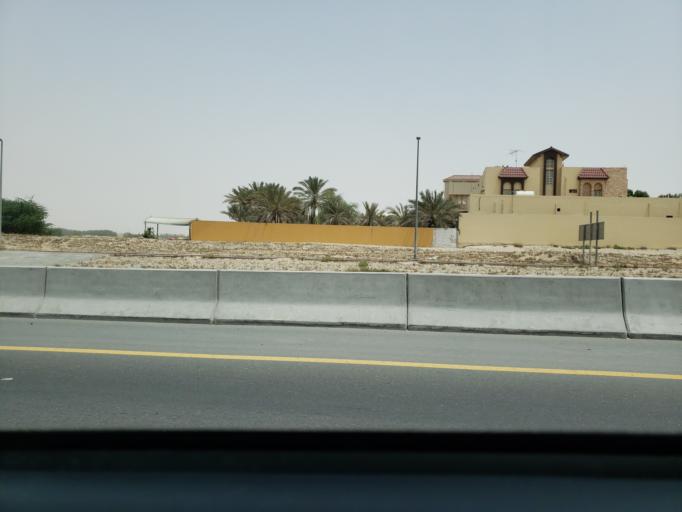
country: AE
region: Ash Shariqah
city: Sharjah
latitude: 25.3387
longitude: 55.4686
